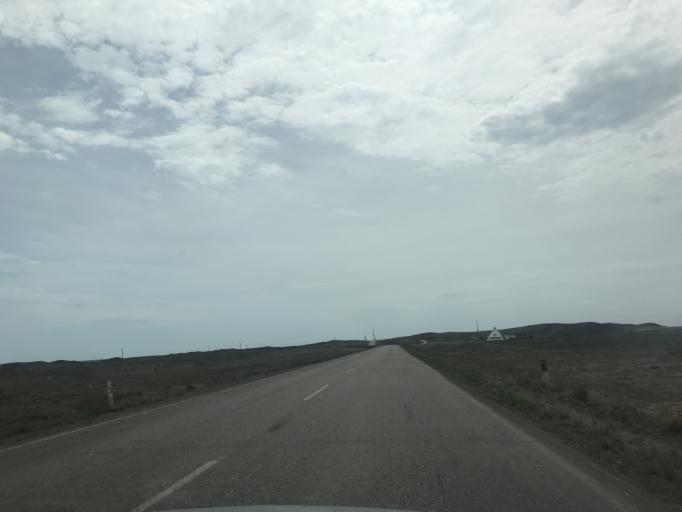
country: KZ
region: Zhambyl
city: Mynaral
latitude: 45.4533
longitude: 73.5968
